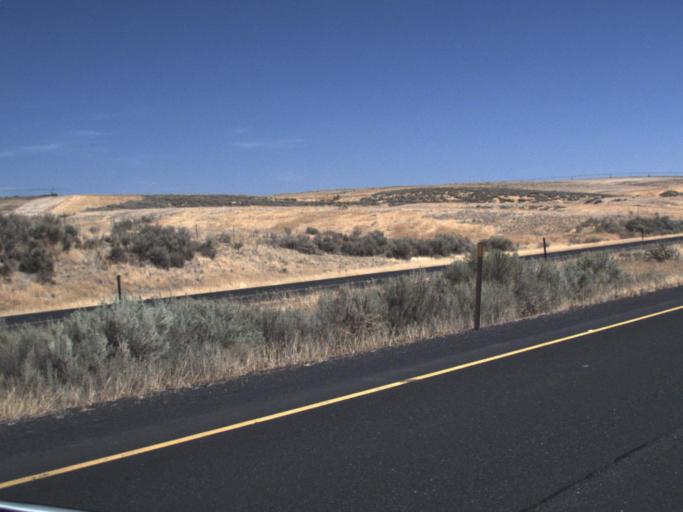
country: US
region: Washington
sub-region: Grant County
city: Warden
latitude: 47.0843
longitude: -118.9755
